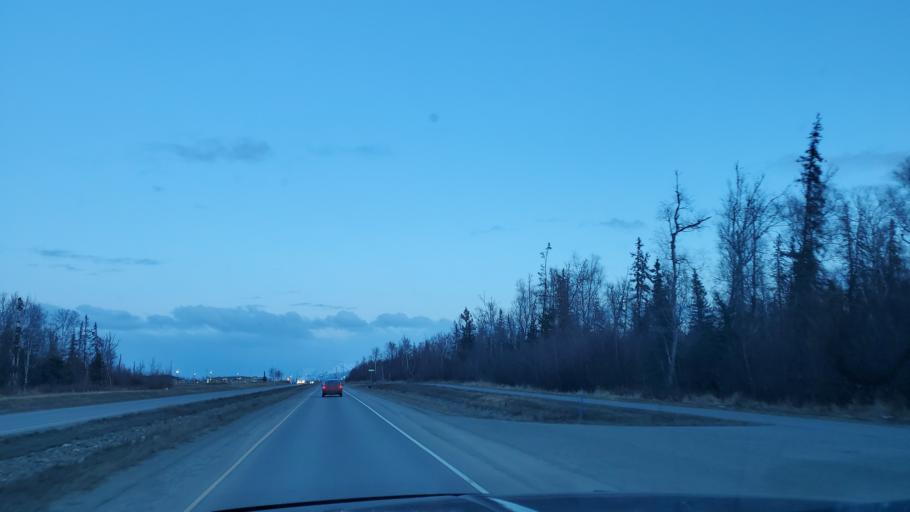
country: US
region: Alaska
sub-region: Matanuska-Susitna Borough
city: Wasilla
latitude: 61.5716
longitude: -149.4312
